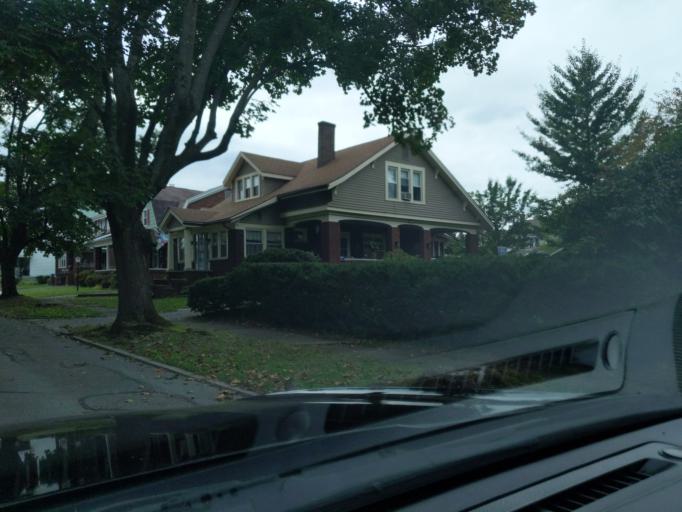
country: US
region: Pennsylvania
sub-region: Blair County
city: Altoona
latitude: 40.4971
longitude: -78.4073
